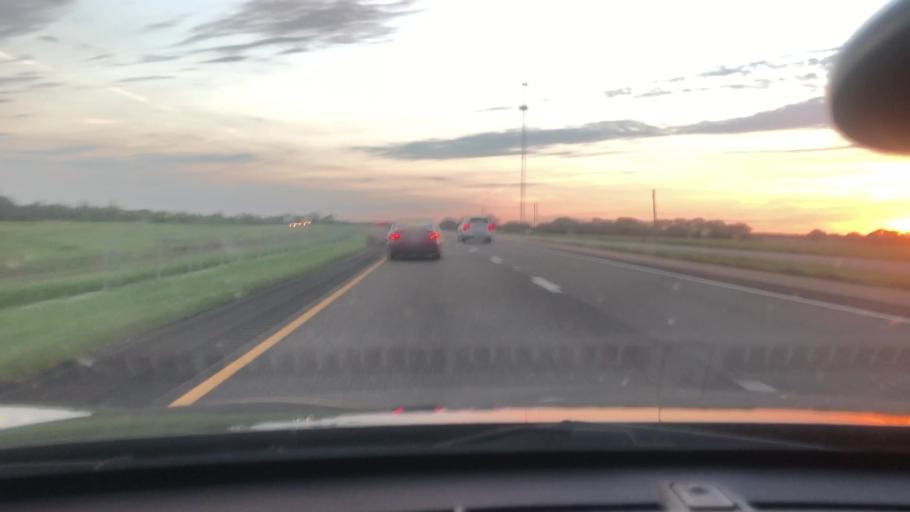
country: US
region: Texas
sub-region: Victoria County
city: Inez
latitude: 28.9268
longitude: -96.7491
